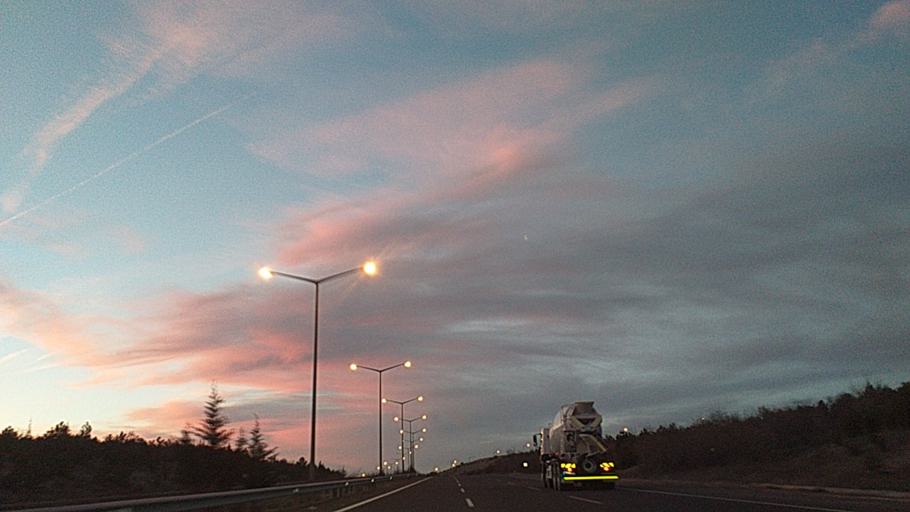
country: TR
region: Ankara
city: Etimesgut
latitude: 40.0176
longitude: 32.6252
